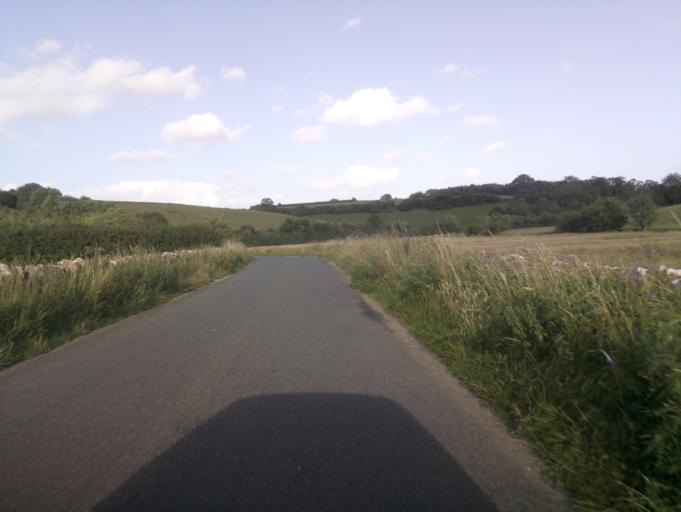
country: GB
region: England
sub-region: Gloucestershire
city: Westfield
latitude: 51.9057
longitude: -1.8176
